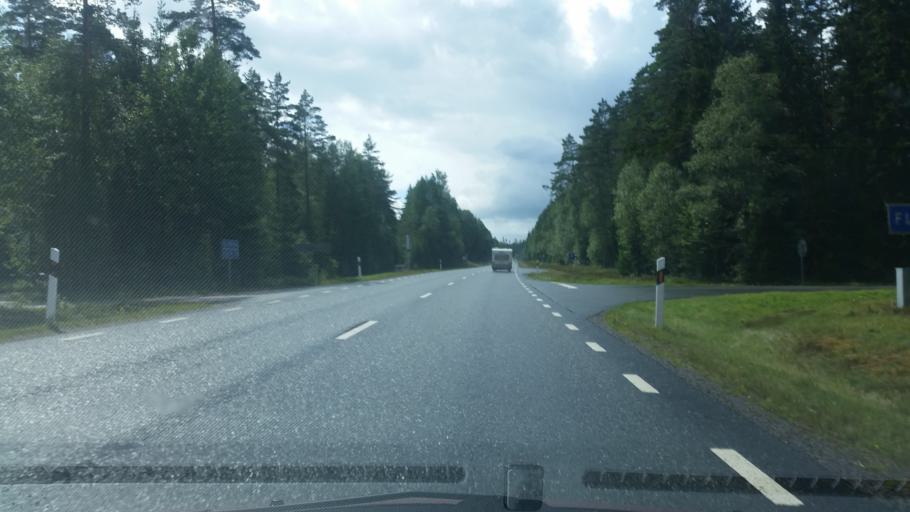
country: SE
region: Joenkoeping
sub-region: Gislaveds Kommun
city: Gislaved
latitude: 57.3880
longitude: 13.5873
